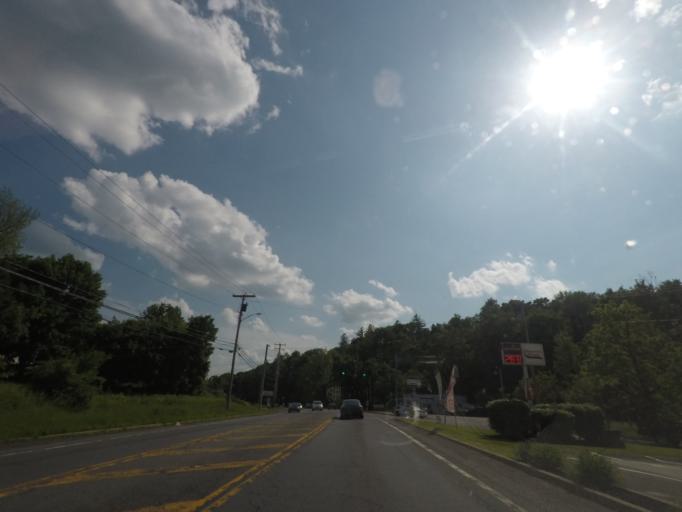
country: US
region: New York
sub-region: Orange County
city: Balmville
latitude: 41.5448
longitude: -74.0111
